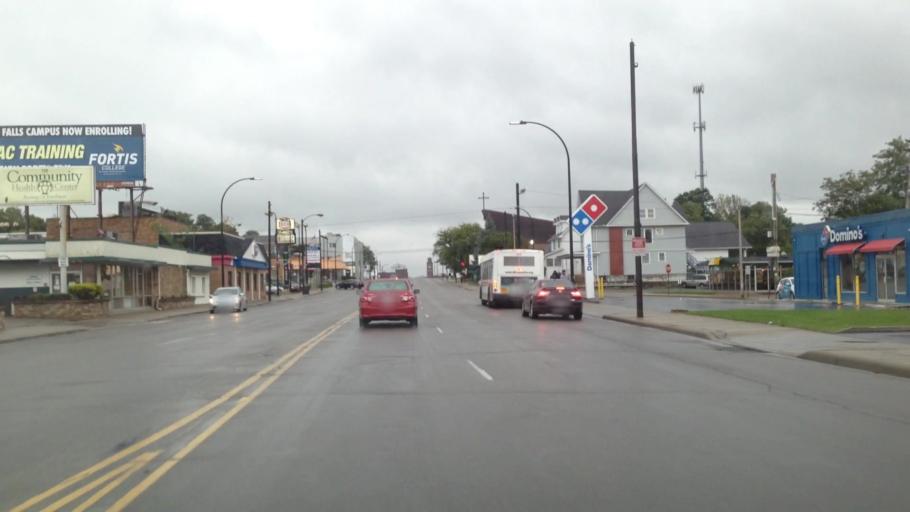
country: US
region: Ohio
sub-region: Summit County
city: Akron
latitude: 41.0761
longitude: -81.4953
